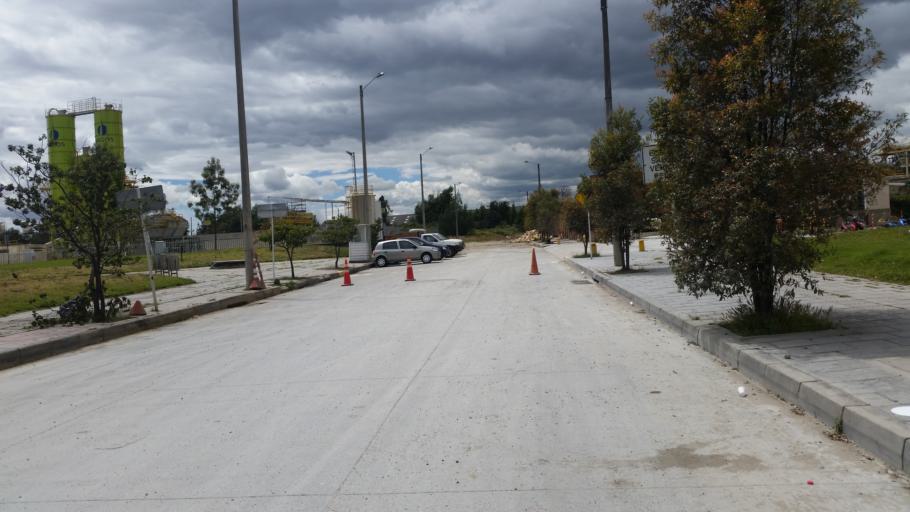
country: CO
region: Bogota D.C.
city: Bogota
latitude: 4.6397
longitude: -74.1077
